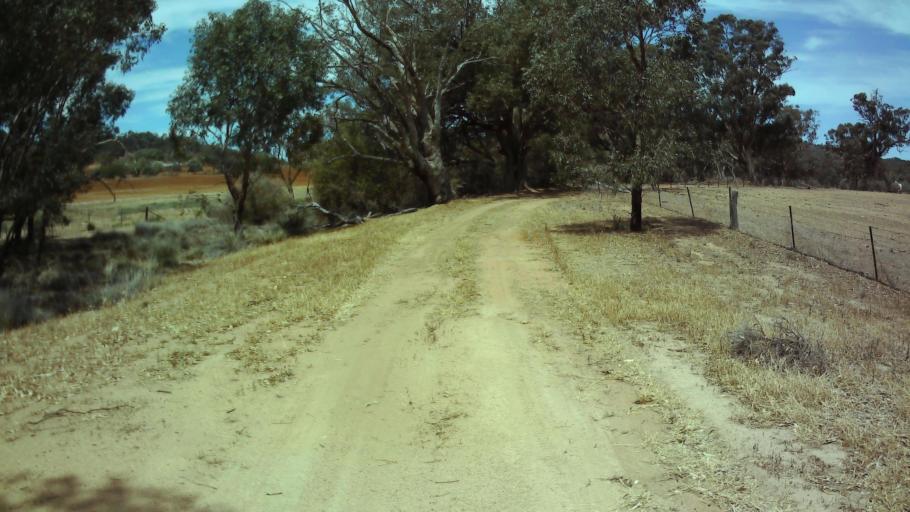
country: AU
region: New South Wales
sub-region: Weddin
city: Grenfell
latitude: -33.7641
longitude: 148.1474
